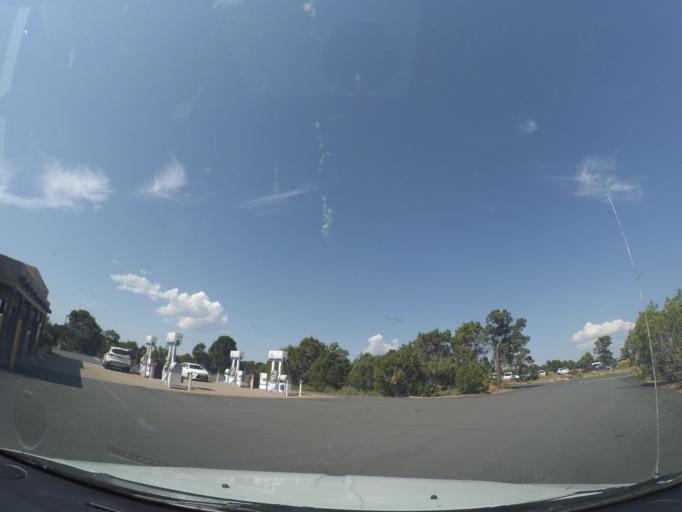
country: US
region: Arizona
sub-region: Coconino County
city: Grand Canyon
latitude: 36.0406
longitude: -111.8262
